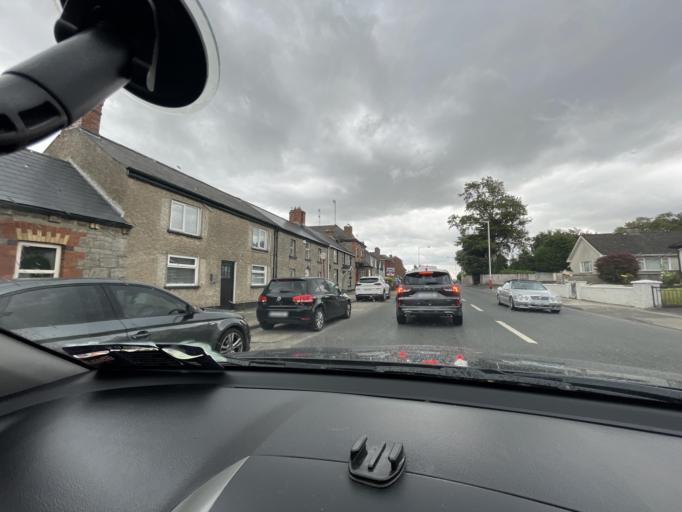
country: IE
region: Leinster
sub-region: Lu
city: Drogheda
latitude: 53.7218
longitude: -6.3599
